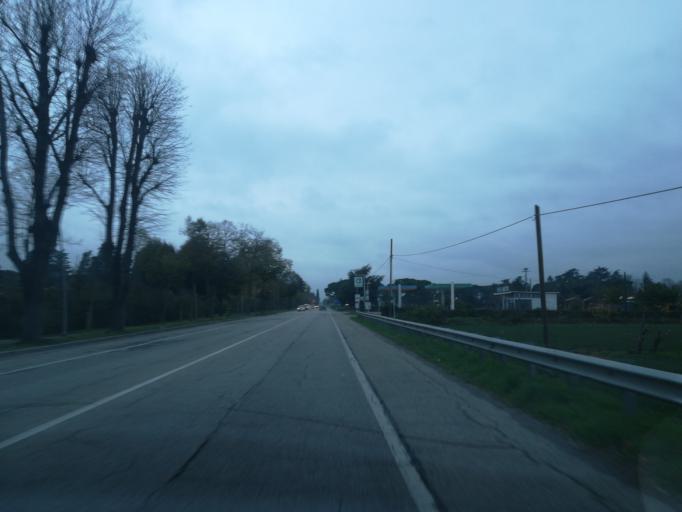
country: IT
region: Emilia-Romagna
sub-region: Provincia di Bologna
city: Imola
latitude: 44.3678
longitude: 11.6776
